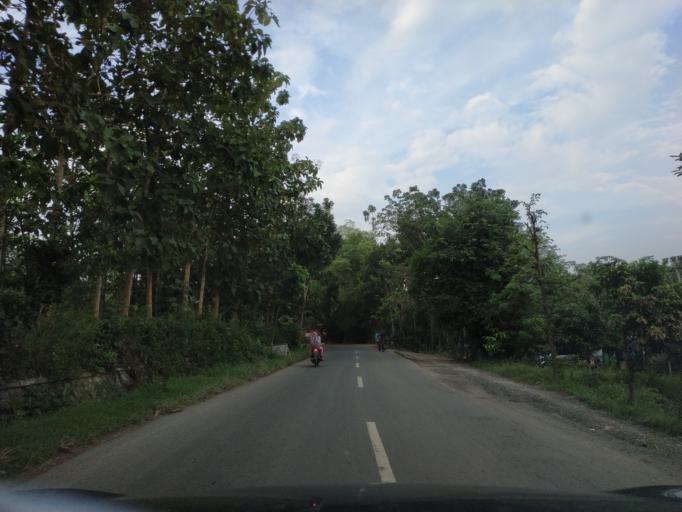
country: ID
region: Central Java
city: Medang
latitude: -6.9039
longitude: 111.4430
